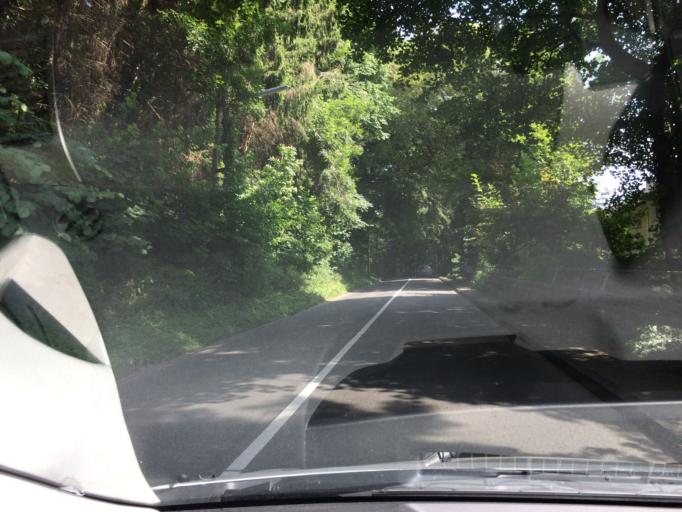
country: DE
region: North Rhine-Westphalia
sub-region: Regierungsbezirk Arnsberg
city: Nachrodt-Wiblingwerde
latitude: 51.3562
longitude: 7.6027
